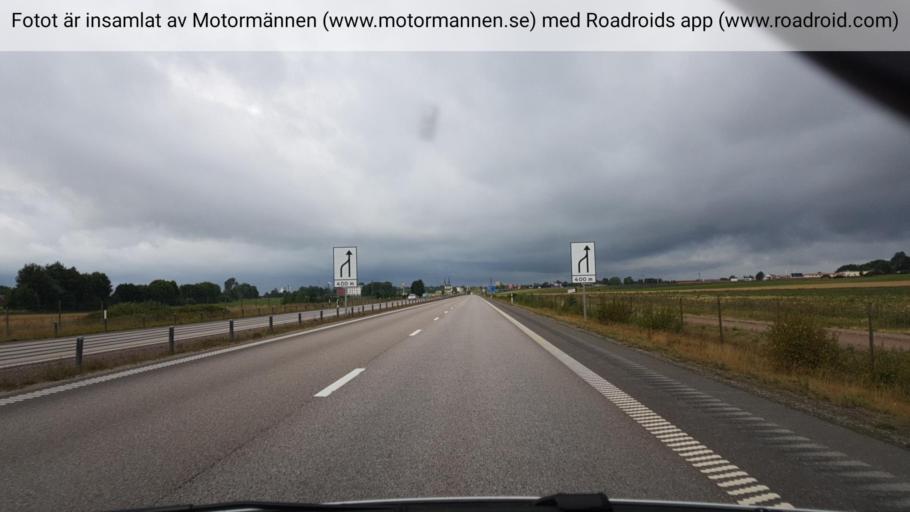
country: SE
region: Vaestra Goetaland
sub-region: Skara Kommun
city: Skara
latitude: 58.3950
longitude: 13.4800
